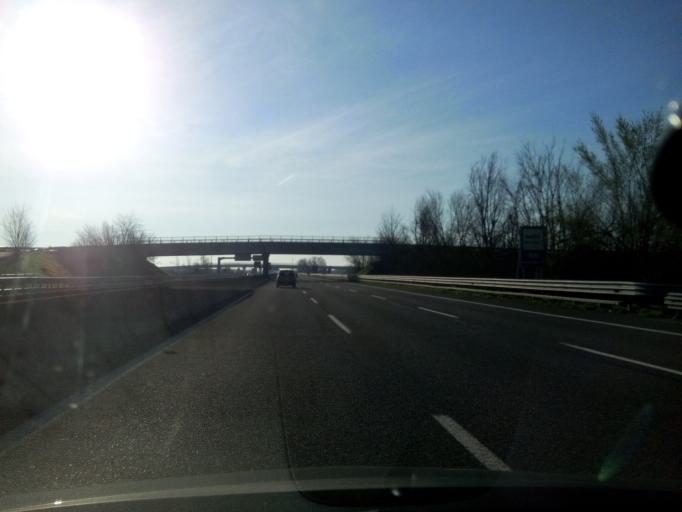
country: IT
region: Emilia-Romagna
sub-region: Provincia di Reggio Emilia
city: Caprara
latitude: 44.7795
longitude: 10.4955
